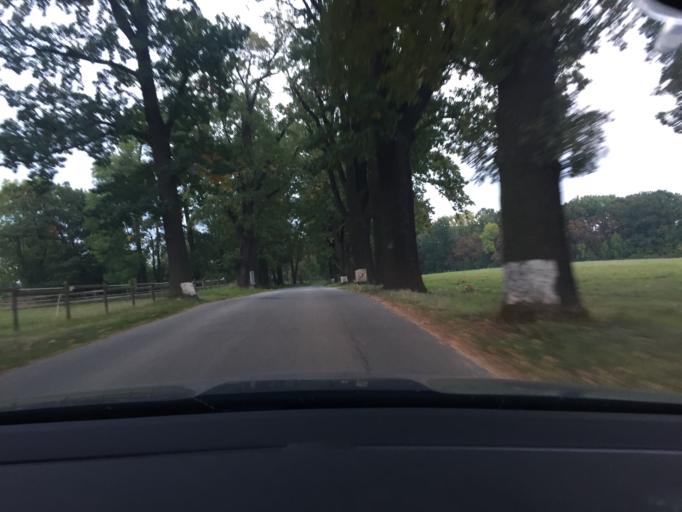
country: CZ
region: Jihocesky
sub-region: Okres Ceske Budejovice
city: Hluboka nad Vltavou
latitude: 49.0387
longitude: 14.4100
